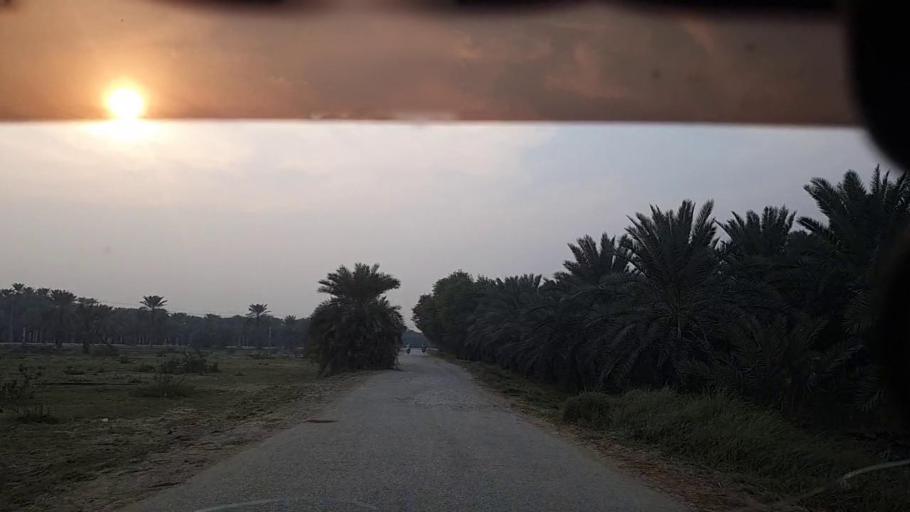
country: PK
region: Sindh
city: Khairpur
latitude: 27.5020
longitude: 68.6889
